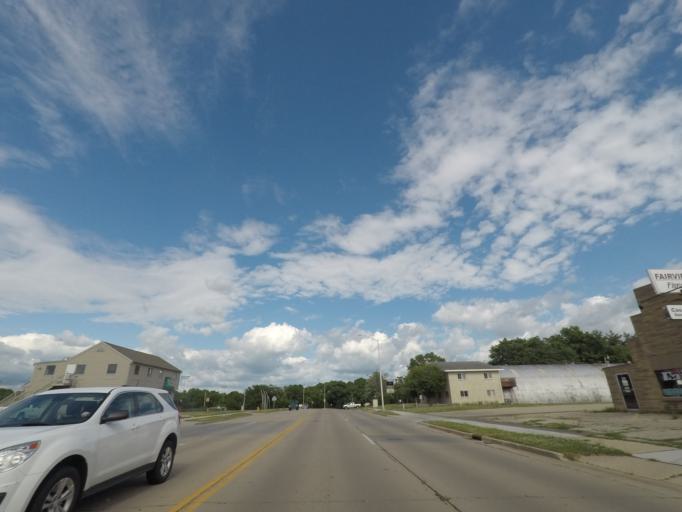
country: US
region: Wisconsin
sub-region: Rock County
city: Janesville
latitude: 42.6789
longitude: -89.0015
